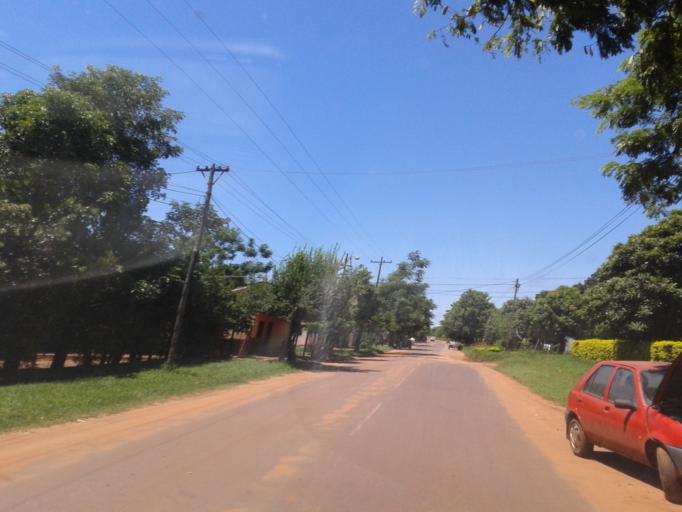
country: PY
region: Misiones
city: Santa Maria
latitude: -26.8956
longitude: -57.0273
